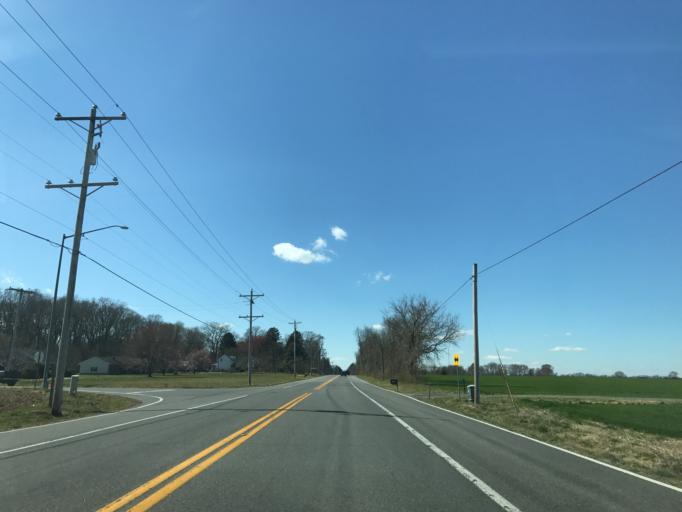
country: US
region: Maryland
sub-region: Kent County
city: Chestertown
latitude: 39.2146
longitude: -76.1127
